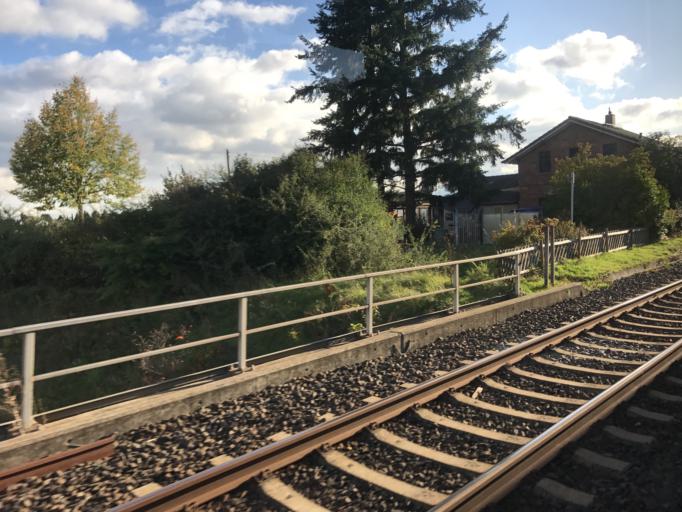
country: DE
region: Hesse
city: Raunheim
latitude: 50.0033
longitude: 8.4431
